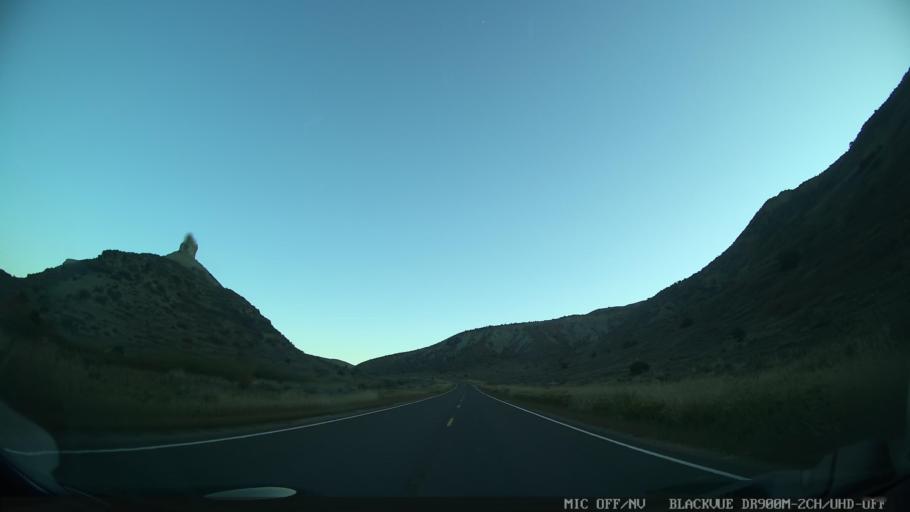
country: US
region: Colorado
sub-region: Eagle County
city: Edwards
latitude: 39.7828
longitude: -106.6788
